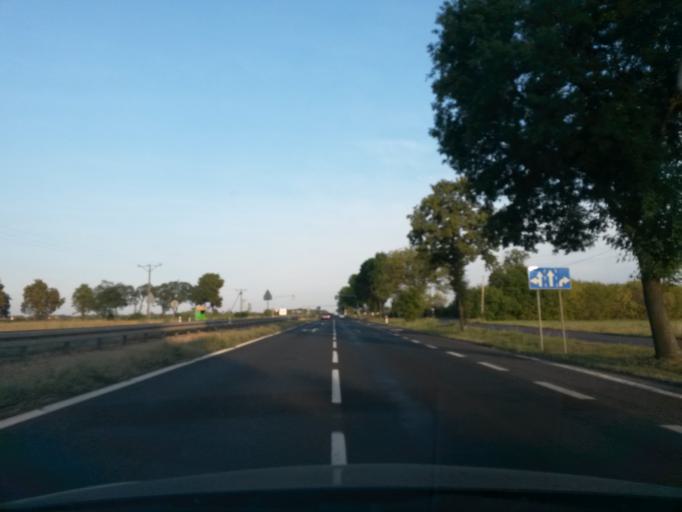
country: PL
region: Masovian Voivodeship
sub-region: Powiat warszawski zachodni
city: Dziekanow Lesny
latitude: 52.3716
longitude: 20.7914
